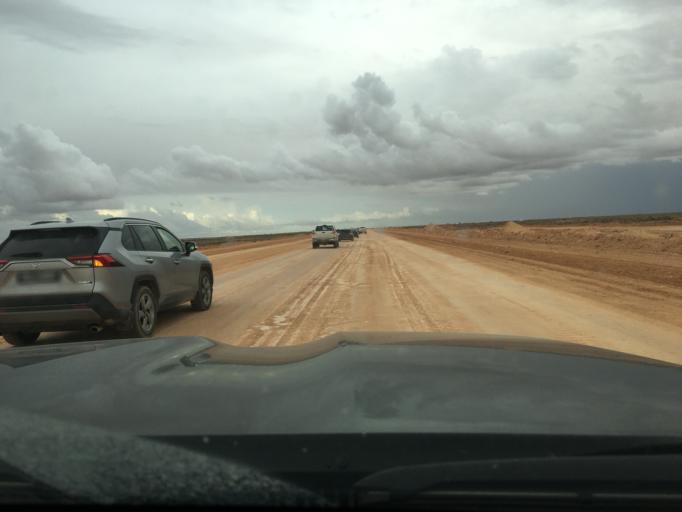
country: TN
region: Madanin
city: Medenine
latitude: 33.2731
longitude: 10.5889
